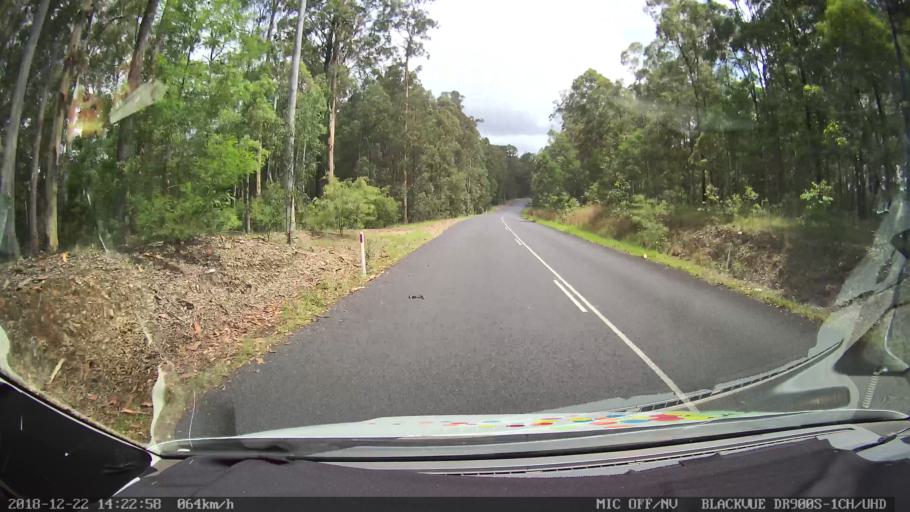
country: AU
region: New South Wales
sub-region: Clarence Valley
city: Coutts Crossing
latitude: -30.0303
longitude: 152.6536
